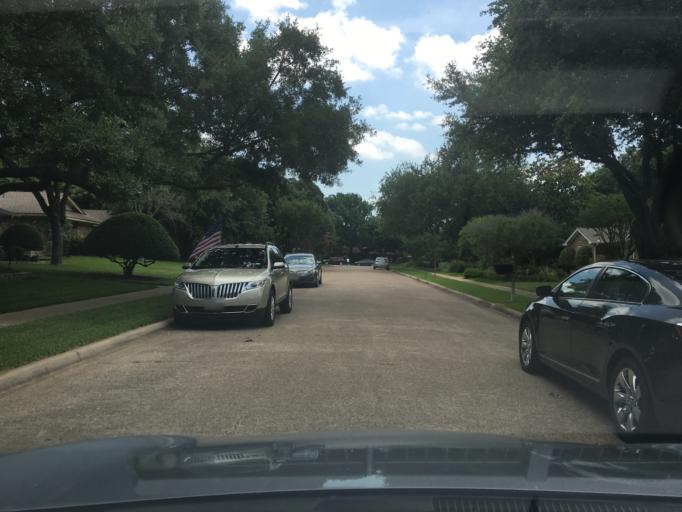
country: US
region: Texas
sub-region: Dallas County
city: Richardson
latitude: 32.9583
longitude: -96.6884
